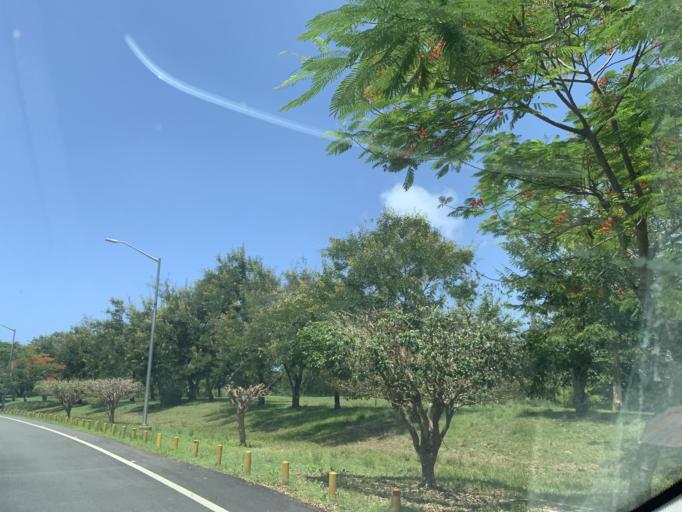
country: DO
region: Puerto Plata
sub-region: Puerto Plata
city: Puerto Plata
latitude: 19.7525
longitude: -70.5616
